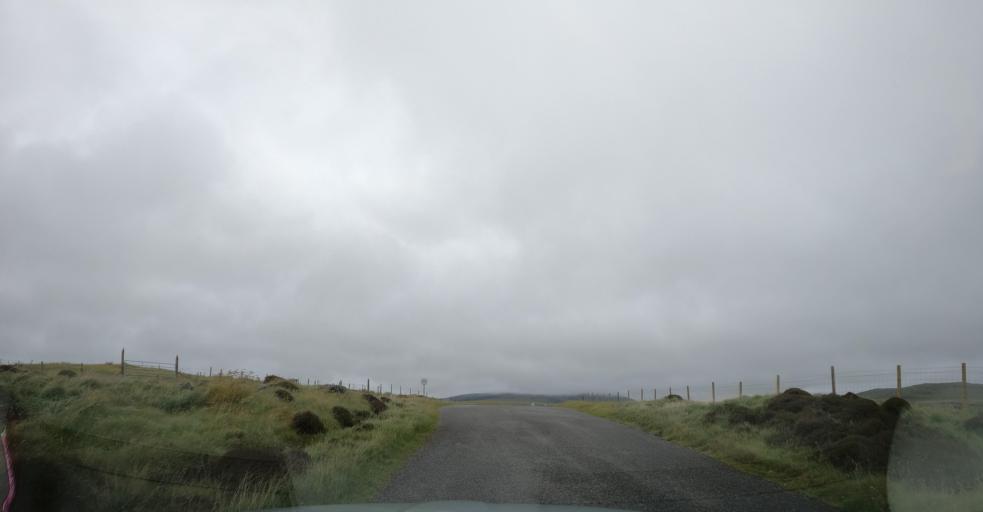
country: GB
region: Scotland
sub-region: Eilean Siar
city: Isle of North Uist
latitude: 57.5843
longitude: -7.4009
